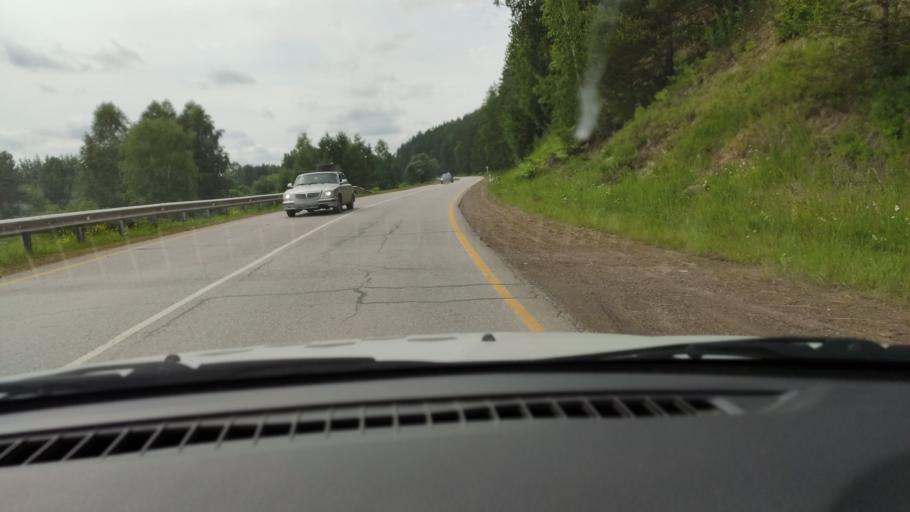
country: RU
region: Perm
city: Kukushtan
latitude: 57.4884
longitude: 56.6281
